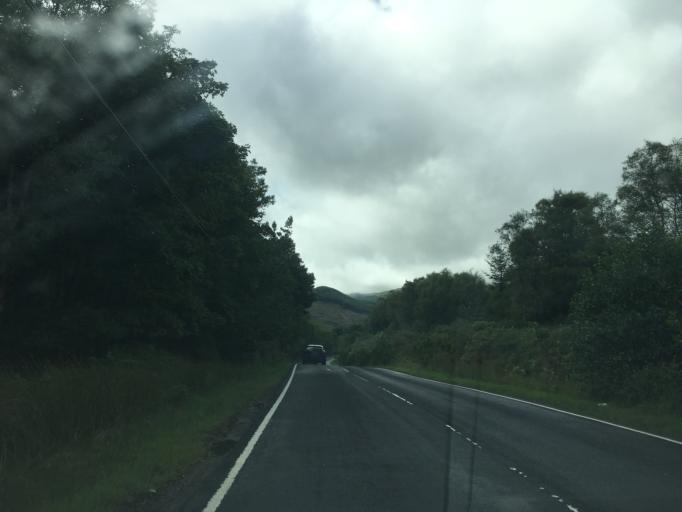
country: GB
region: Scotland
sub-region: Argyll and Bute
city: Dunoon
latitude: 55.9904
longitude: -5.0071
